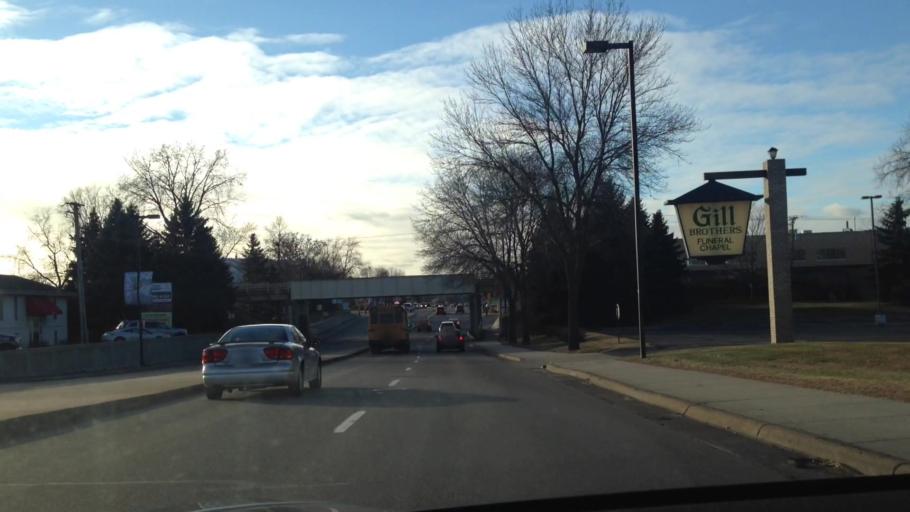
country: US
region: Minnesota
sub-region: Hennepin County
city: Crystal
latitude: 45.0330
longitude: -93.3738
